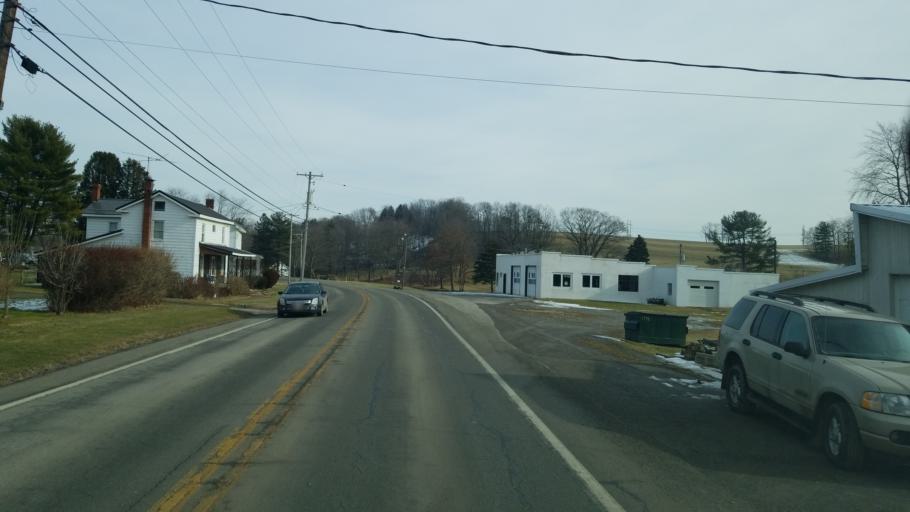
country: US
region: Pennsylvania
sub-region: Cambria County
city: Barnesboro
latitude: 40.7517
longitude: -78.8788
